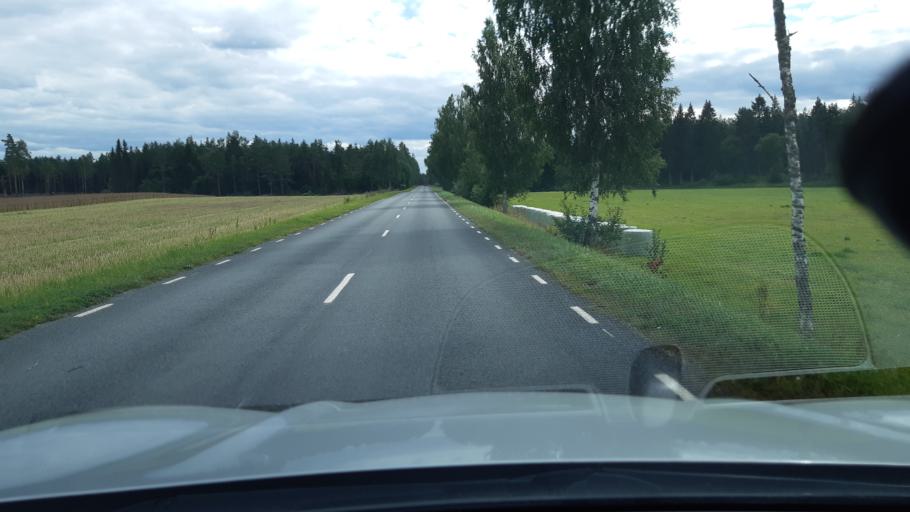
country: EE
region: Raplamaa
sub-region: Maerjamaa vald
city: Marjamaa
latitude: 59.0357
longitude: 24.5516
